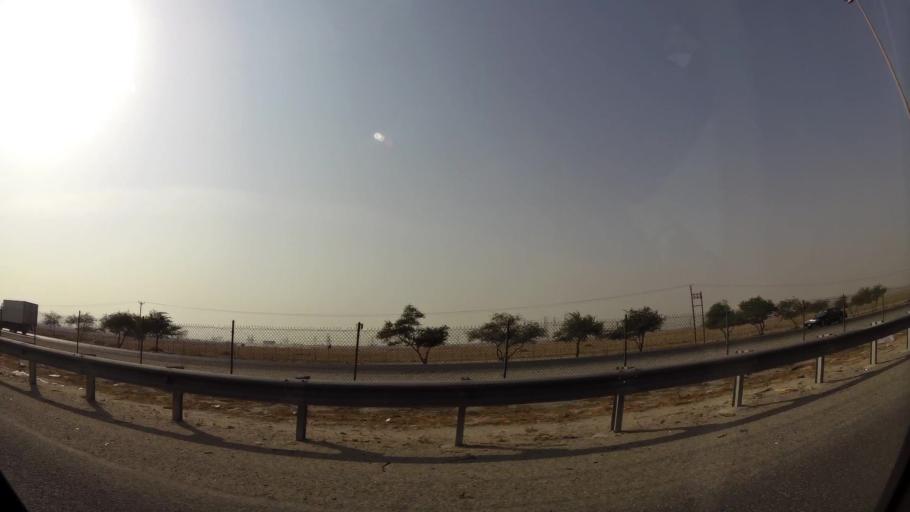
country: KW
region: Al Farwaniyah
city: Janub as Surrah
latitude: 29.1807
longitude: 47.9832
